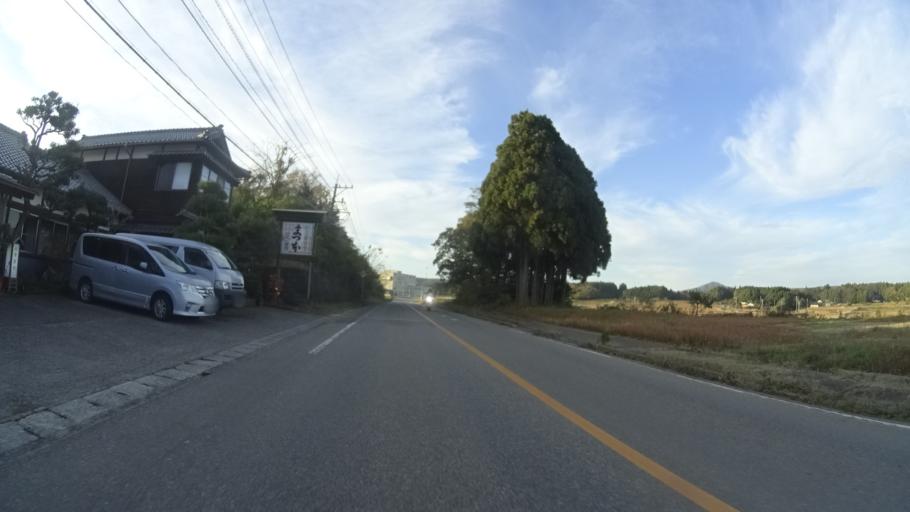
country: JP
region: Ishikawa
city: Nanao
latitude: 37.1577
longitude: 136.7184
